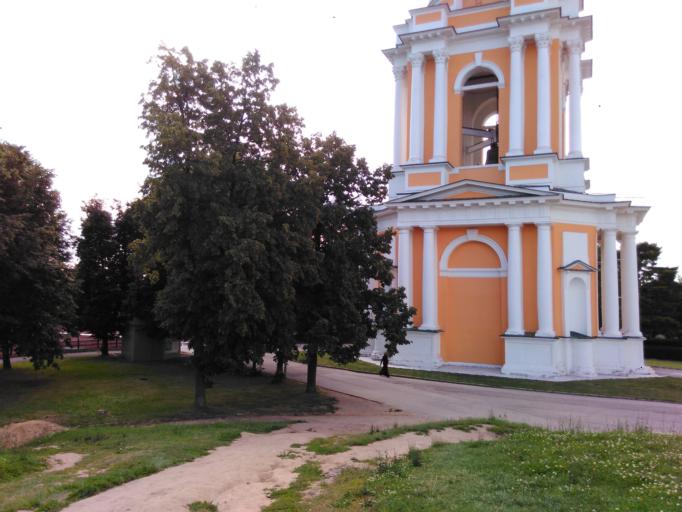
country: RU
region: Rjazan
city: Ryazan'
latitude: 54.6352
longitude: 39.7484
